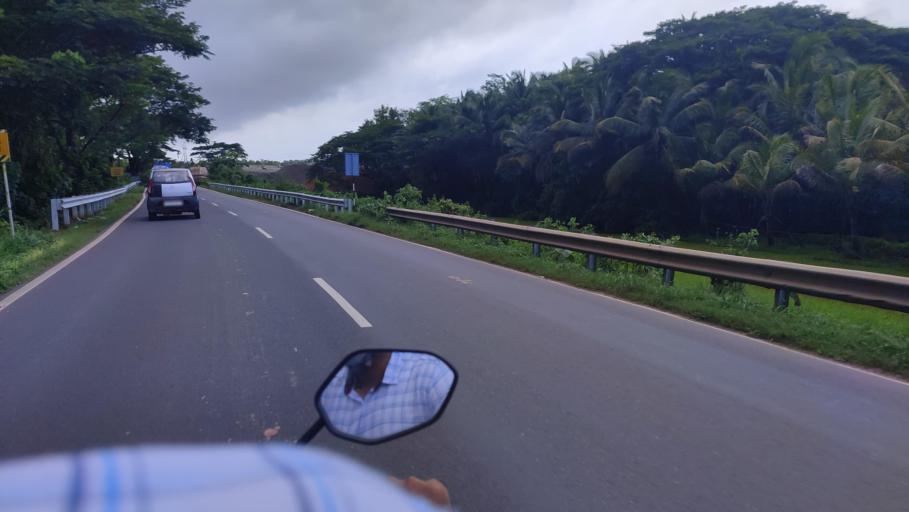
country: IN
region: Kerala
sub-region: Kasaragod District
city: Nileshwar
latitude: 12.2399
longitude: 75.1497
